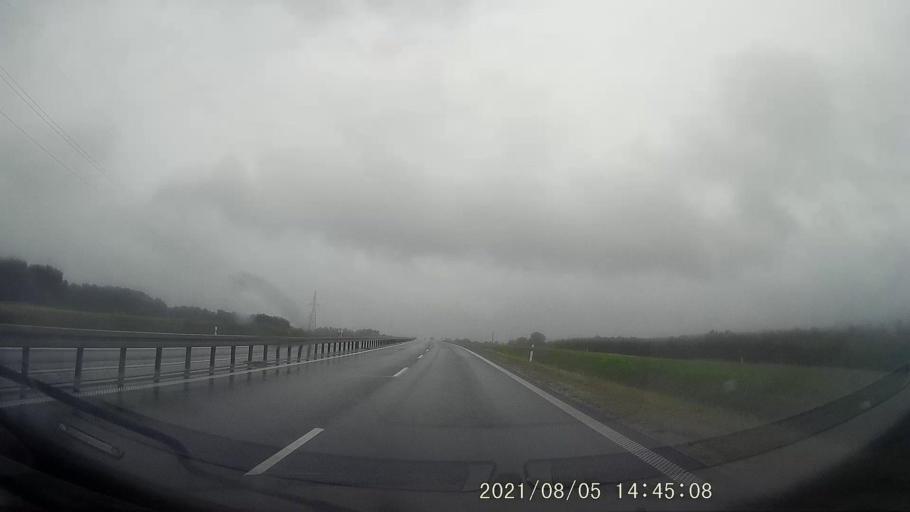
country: PL
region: Opole Voivodeship
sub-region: Powiat nyski
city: Nysa
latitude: 50.4982
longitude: 17.3659
